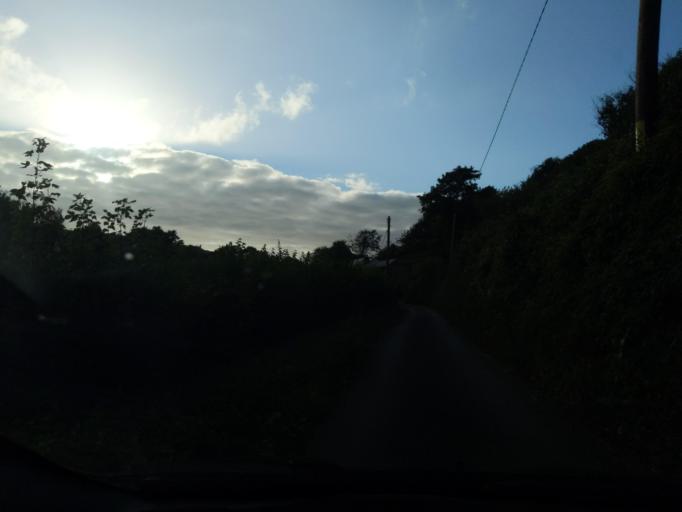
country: GB
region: England
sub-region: Devon
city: Salcombe
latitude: 50.2297
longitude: -3.7946
